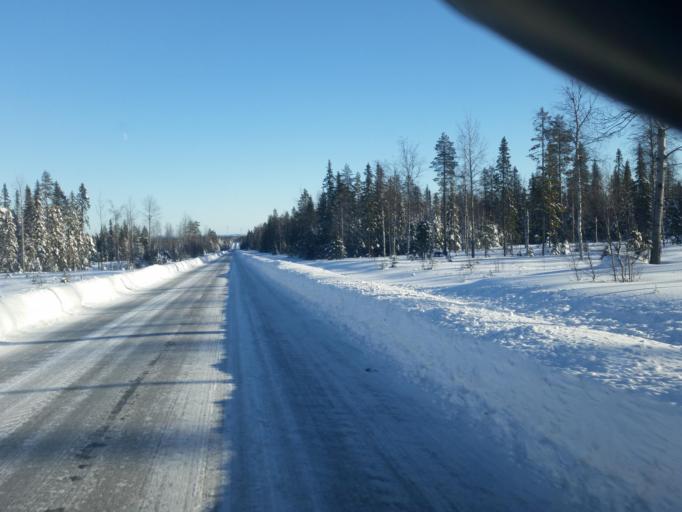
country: SE
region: Vaesterbotten
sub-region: Skelleftea Kommun
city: Storvik
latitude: 65.3253
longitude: 20.7915
